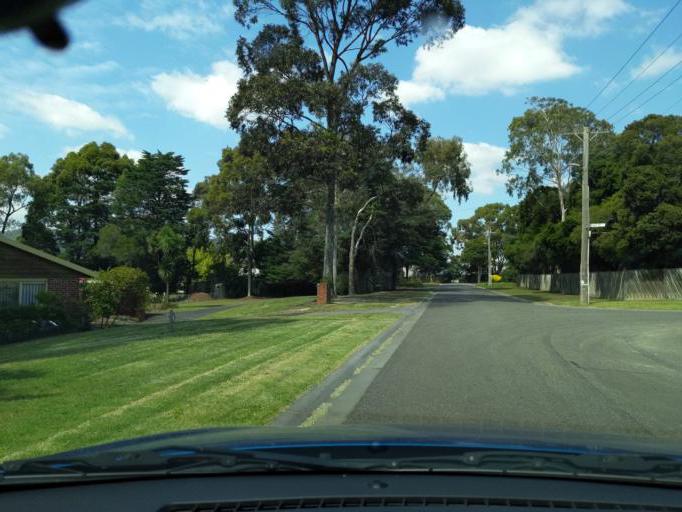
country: AU
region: Victoria
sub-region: Knox
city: Rowville
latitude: -37.9242
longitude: 145.2509
